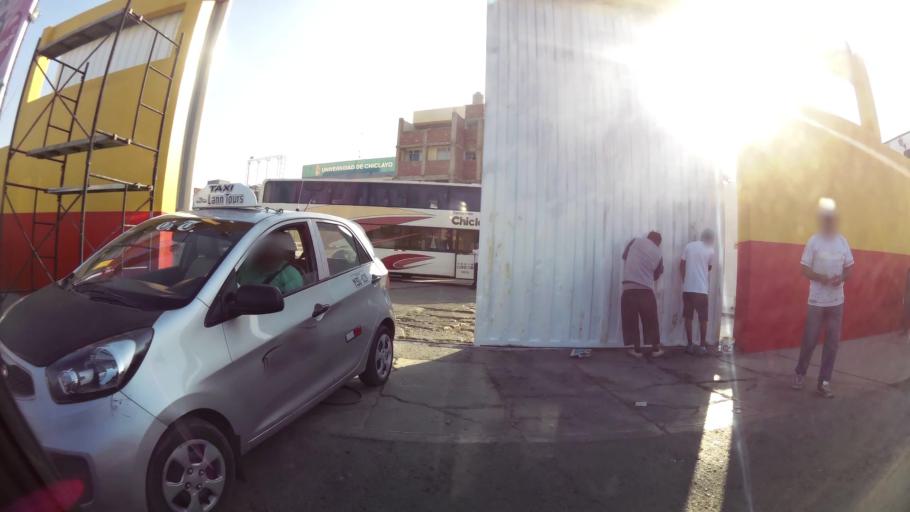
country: PE
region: Lambayeque
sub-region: Provincia de Chiclayo
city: Chiclayo
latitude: -6.7704
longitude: -79.8453
